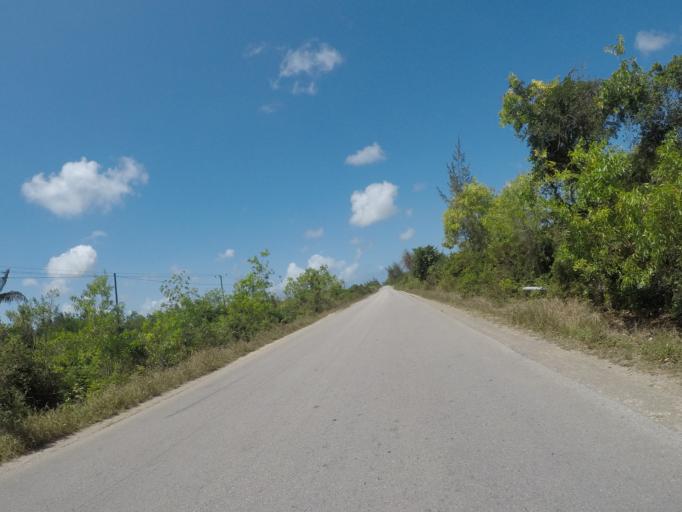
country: TZ
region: Zanzibar Central/South
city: Nganane
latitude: -6.2832
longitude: 39.4662
